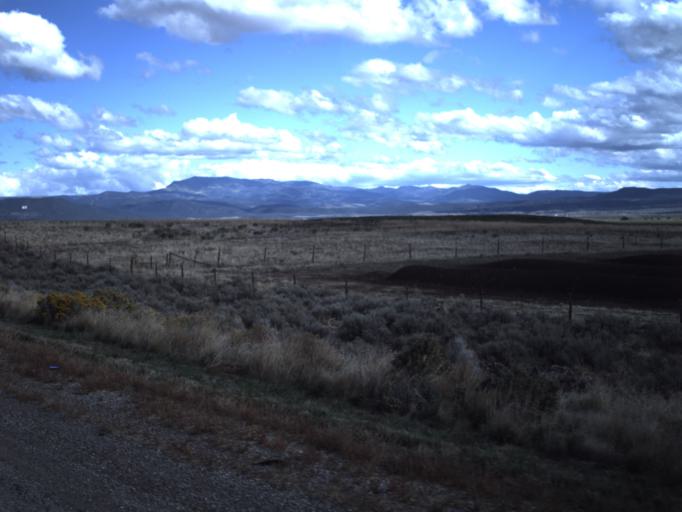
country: US
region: Utah
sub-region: Beaver County
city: Beaver
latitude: 38.2735
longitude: -112.7244
